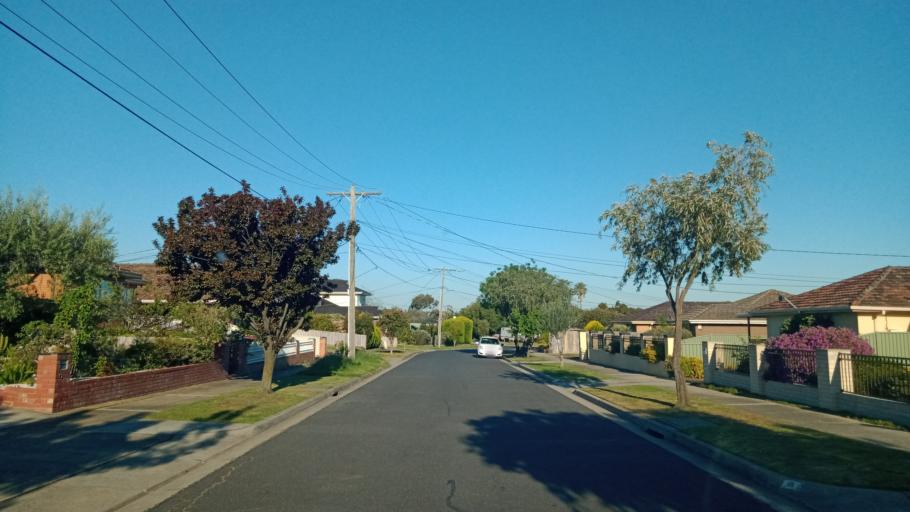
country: AU
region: Victoria
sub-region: Greater Dandenong
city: Springvale
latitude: -37.9318
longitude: 145.1732
